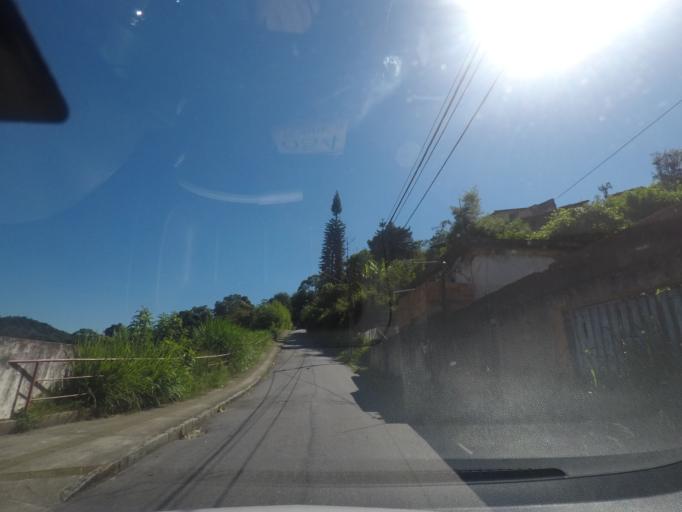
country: BR
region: Rio de Janeiro
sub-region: Petropolis
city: Petropolis
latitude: -22.5118
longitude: -43.1884
